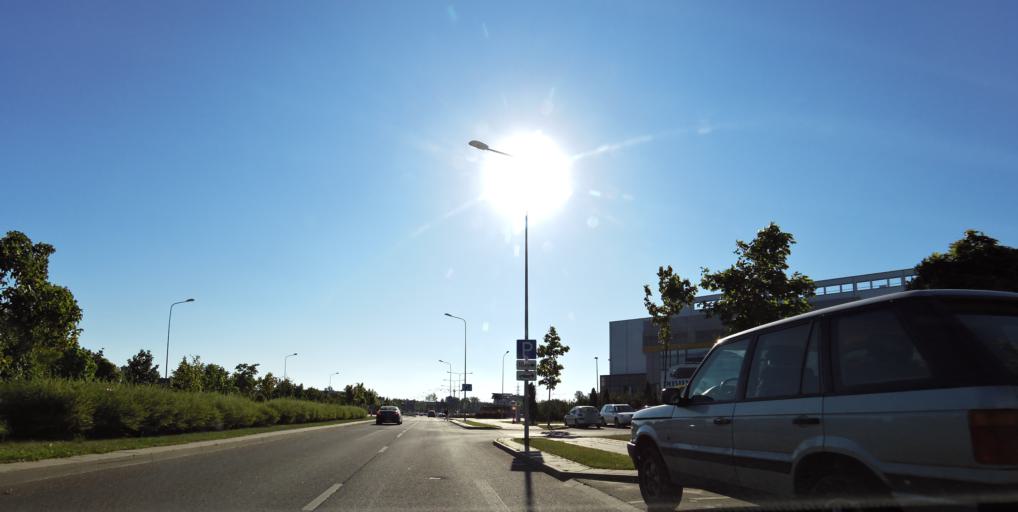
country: LT
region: Vilnius County
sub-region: Vilnius
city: Vilnius
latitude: 54.7172
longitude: 25.2786
